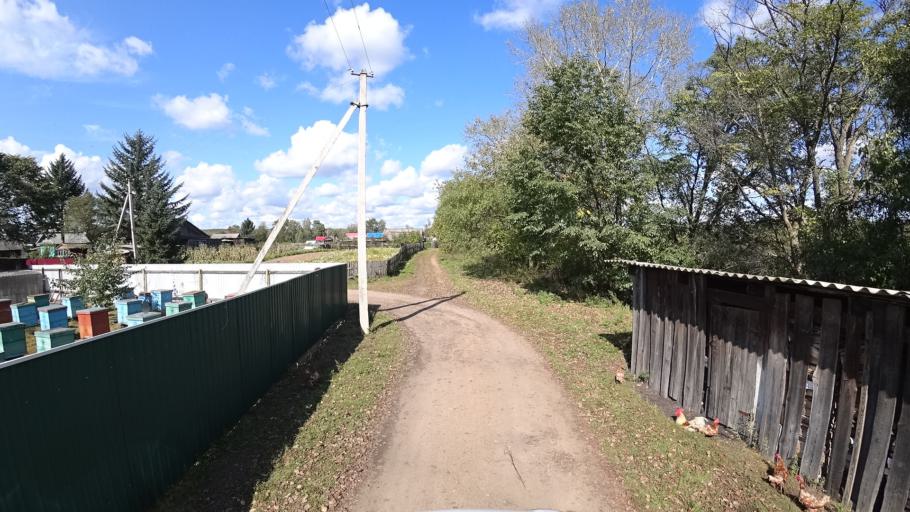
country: RU
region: Amur
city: Arkhara
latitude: 49.4029
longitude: 130.1557
